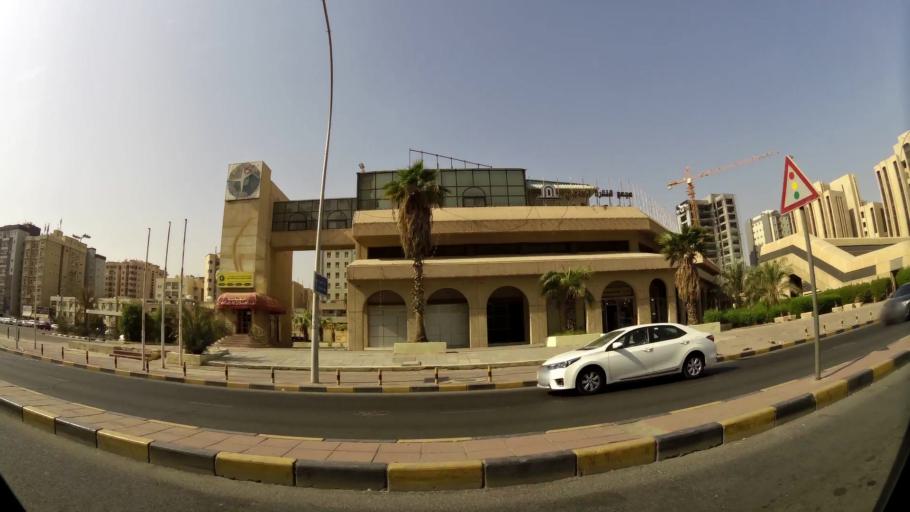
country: KW
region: Muhafazat Hawalli
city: Hawalli
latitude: 29.3318
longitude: 48.0099
